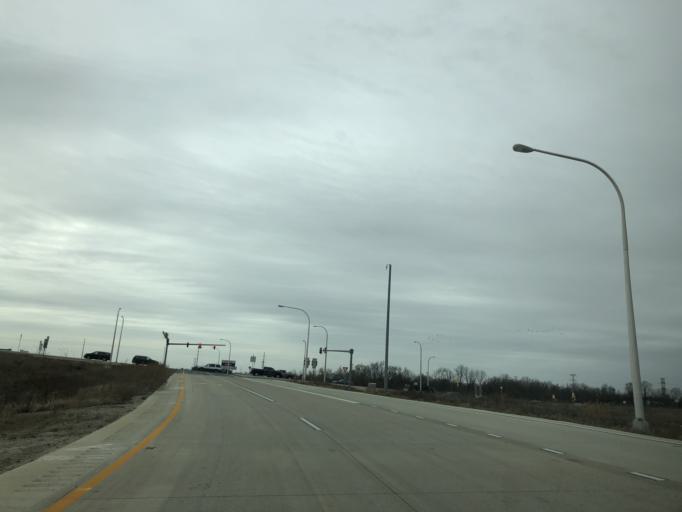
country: US
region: Delaware
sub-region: New Castle County
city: Middletown
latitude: 39.4463
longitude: -75.7521
